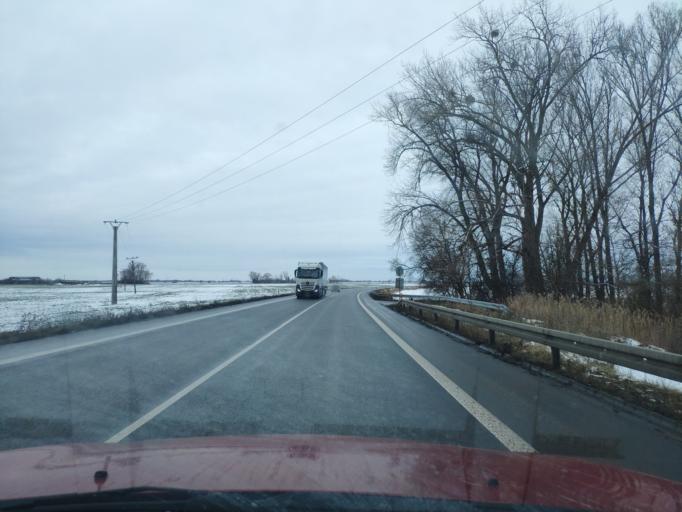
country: SK
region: Trnavsky
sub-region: Okres Galanta
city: Galanta
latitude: 48.1769
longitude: 17.7170
